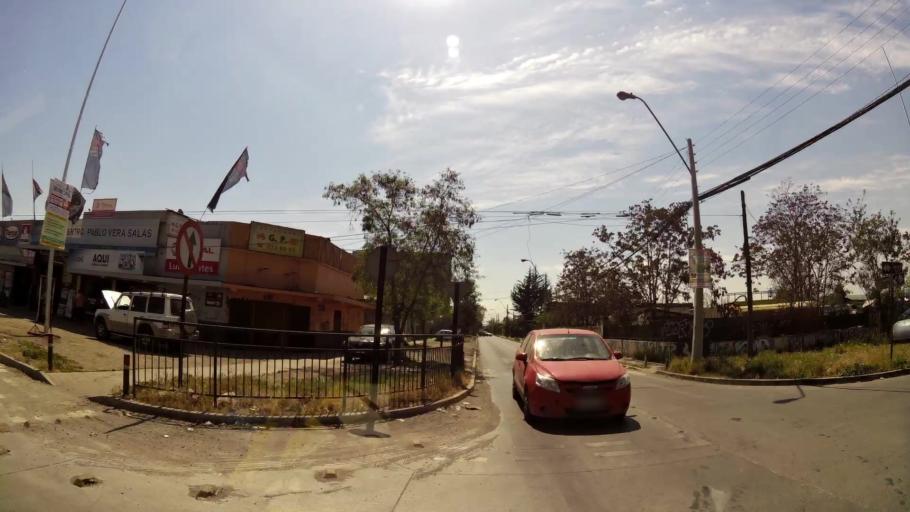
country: CL
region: Santiago Metropolitan
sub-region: Provincia de Santiago
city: La Pintana
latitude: -33.5439
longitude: -70.6581
